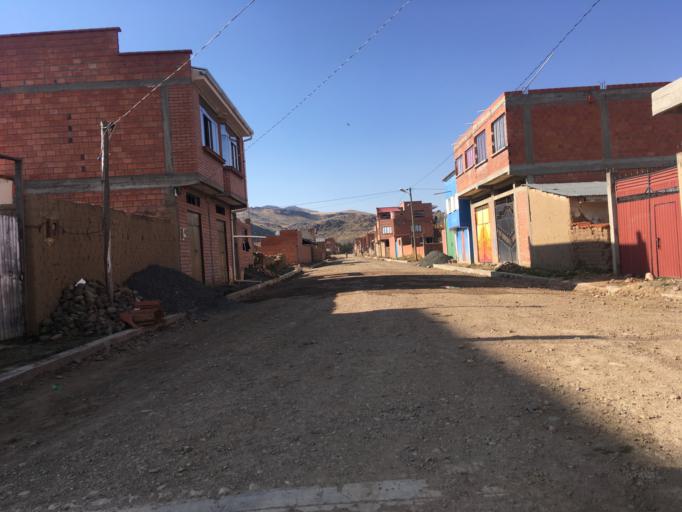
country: BO
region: La Paz
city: Huatajata
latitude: -16.1920
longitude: -68.7441
